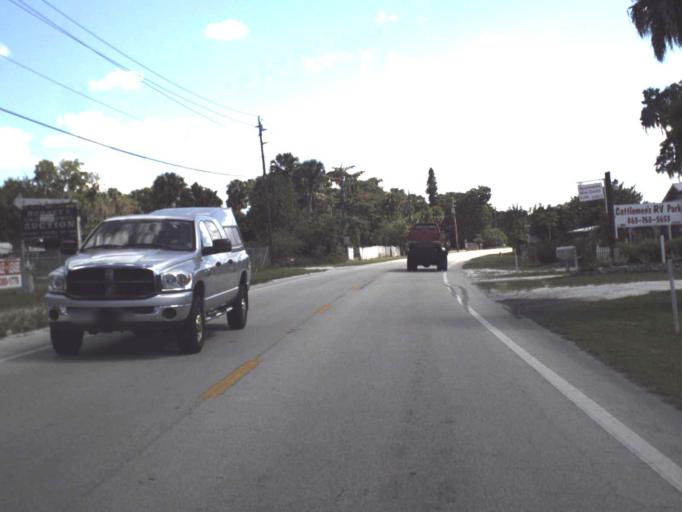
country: US
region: Florida
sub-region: Okeechobee County
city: Taylor Creek
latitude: 27.2090
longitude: -80.7879
